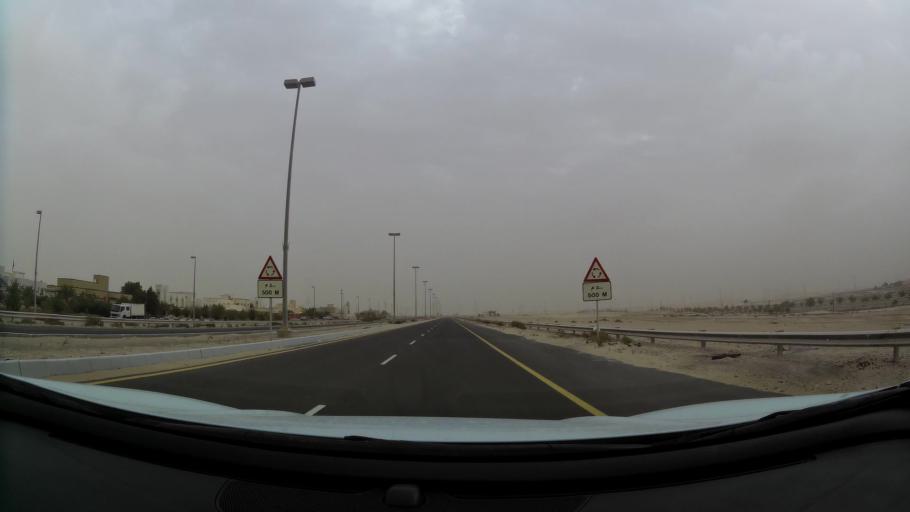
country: AE
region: Abu Dhabi
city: Abu Dhabi
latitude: 24.4213
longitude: 54.7515
